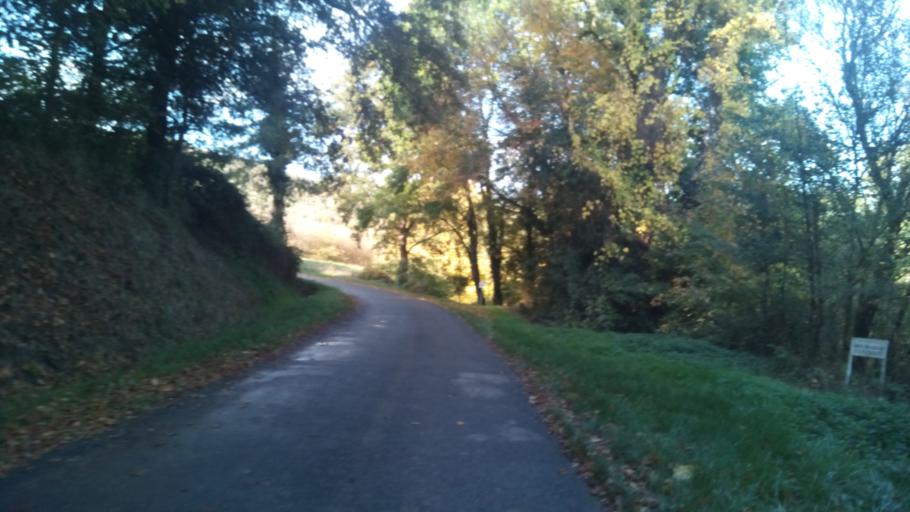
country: FR
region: Midi-Pyrenees
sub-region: Departement du Lot
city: Cajarc
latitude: 44.4716
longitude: 1.8302
